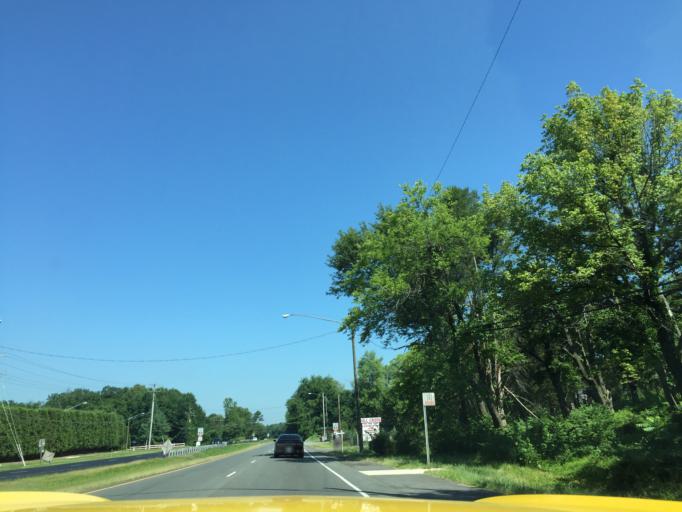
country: US
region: Virginia
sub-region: Fairfax County
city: Wolf Trap
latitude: 38.9456
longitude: -77.2577
